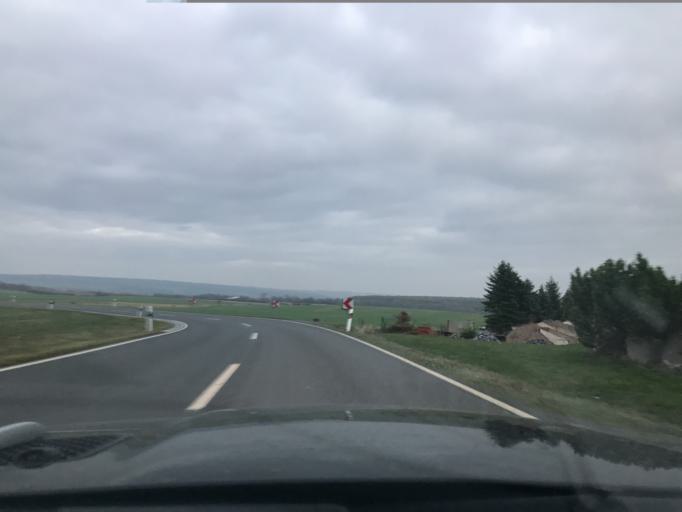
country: DE
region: Thuringia
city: Kullstedt
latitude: 51.2784
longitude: 10.2868
